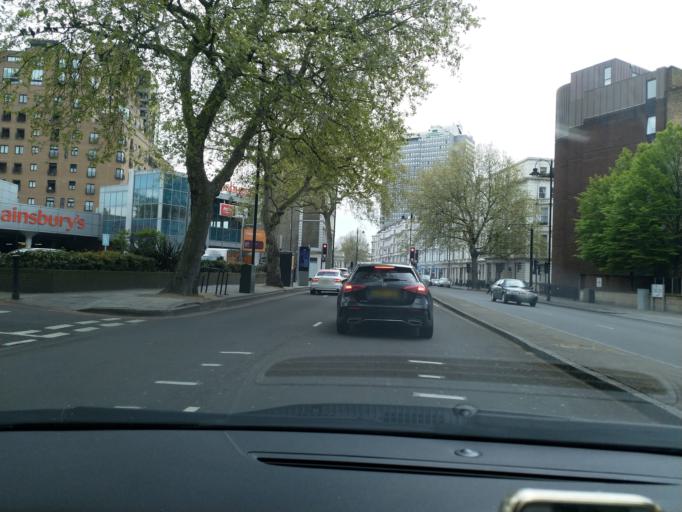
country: GB
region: England
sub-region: Greater London
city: Kensington
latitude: 51.4947
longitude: -0.1896
